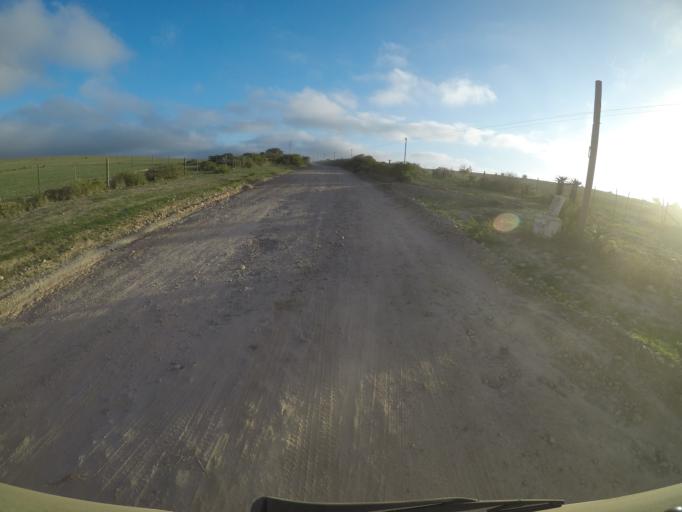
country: ZA
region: Western Cape
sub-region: Eden District Municipality
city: Mossel Bay
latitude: -34.1109
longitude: 22.0543
